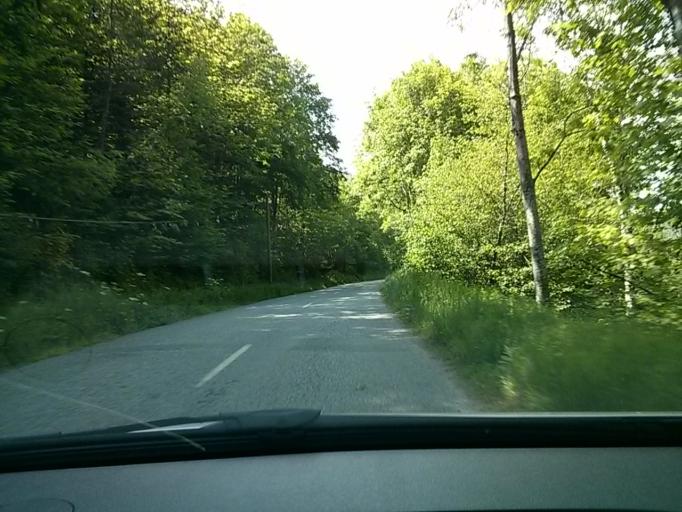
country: FR
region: Rhone-Alpes
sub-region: Departement de la Loire
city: Saint-Chamond
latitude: 45.4151
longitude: 4.5333
